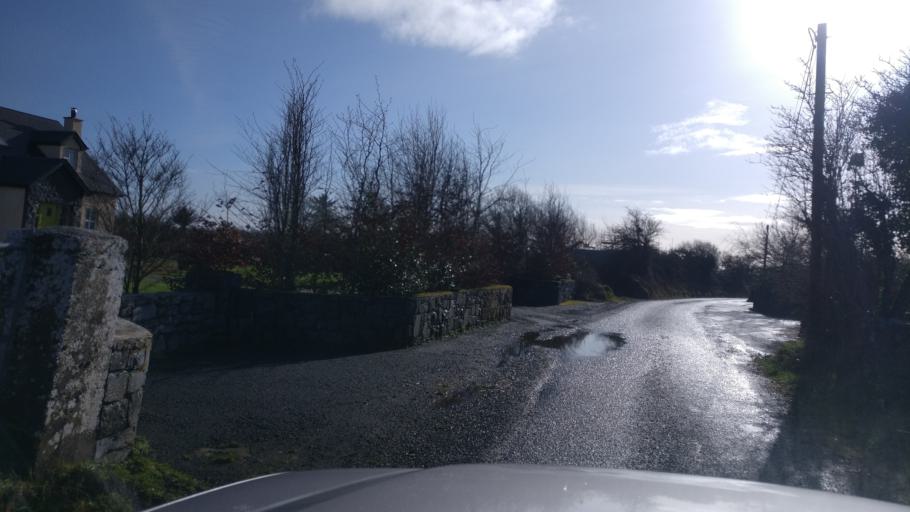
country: IE
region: Connaught
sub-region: County Galway
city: Athenry
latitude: 53.2382
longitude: -8.7795
